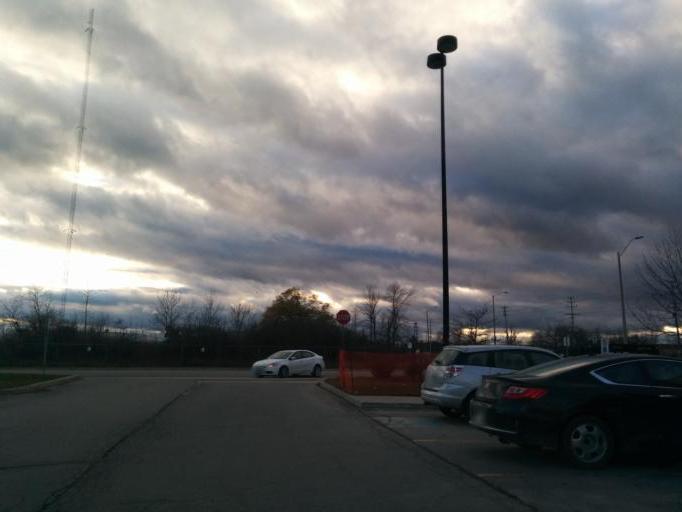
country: CA
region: Ontario
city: Mississauga
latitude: 43.5079
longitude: -79.6323
